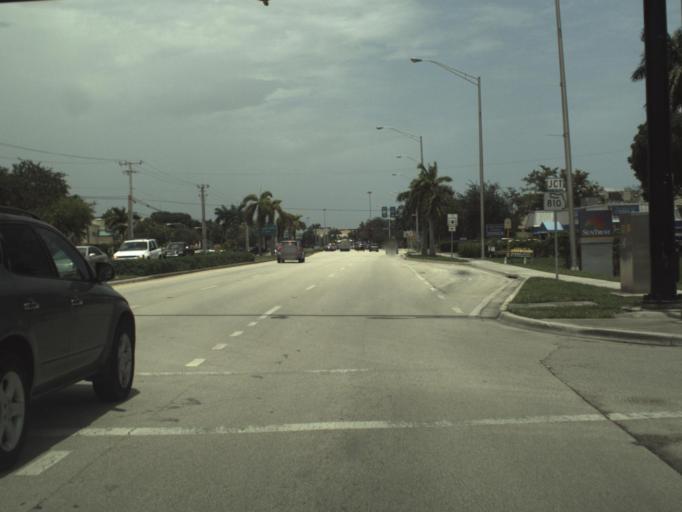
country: US
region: Florida
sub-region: Broward County
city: Deerfield Beach
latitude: 26.3154
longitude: -80.0910
